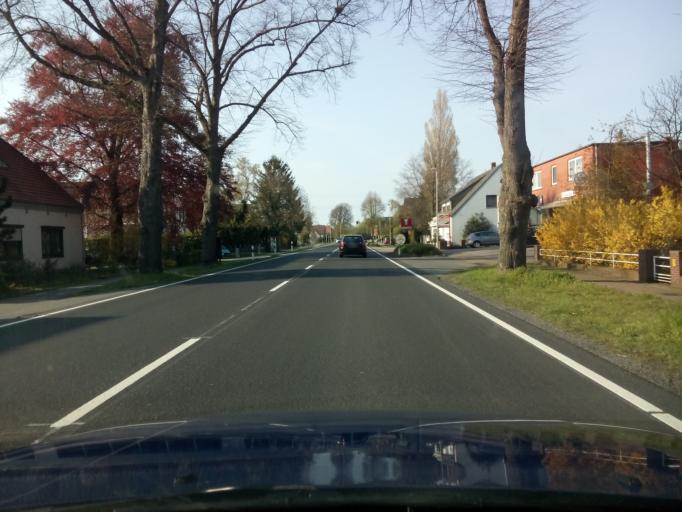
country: DE
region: Lower Saxony
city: Stuhr
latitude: 52.9949
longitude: 8.7868
